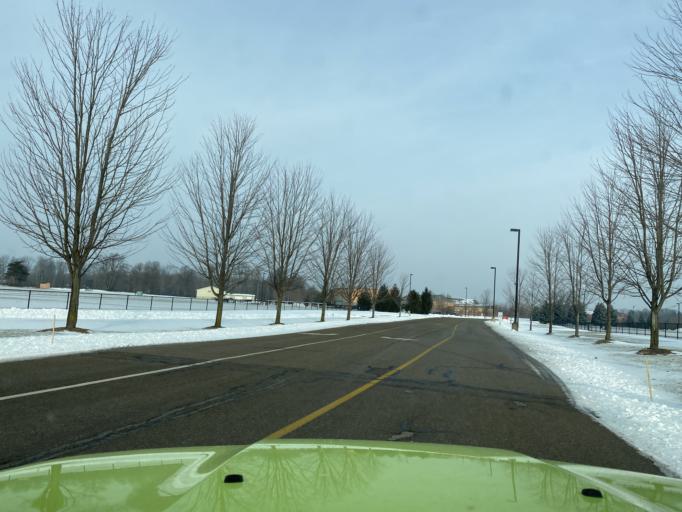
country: US
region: Michigan
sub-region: Ottawa County
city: Allendale
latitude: 42.9578
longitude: -85.9661
